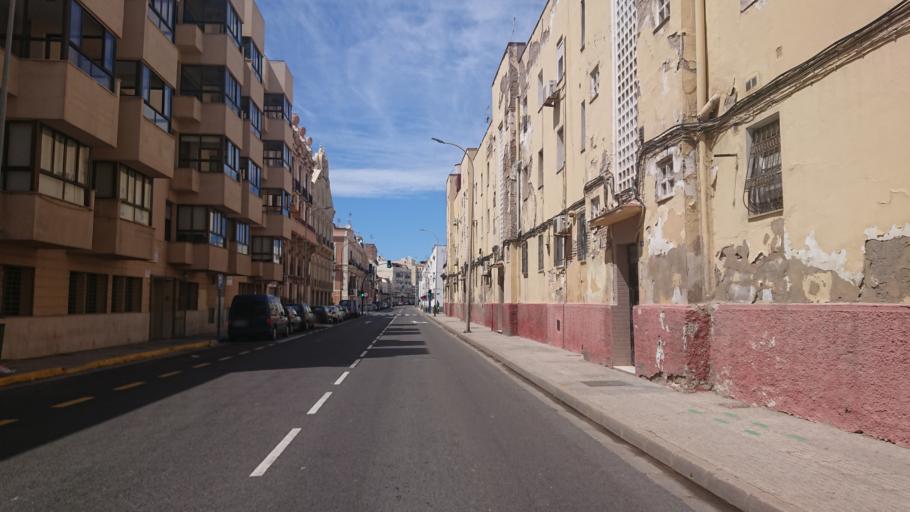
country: ES
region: Melilla
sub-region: Melilla
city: Melilla
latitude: 35.2828
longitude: -2.9410
